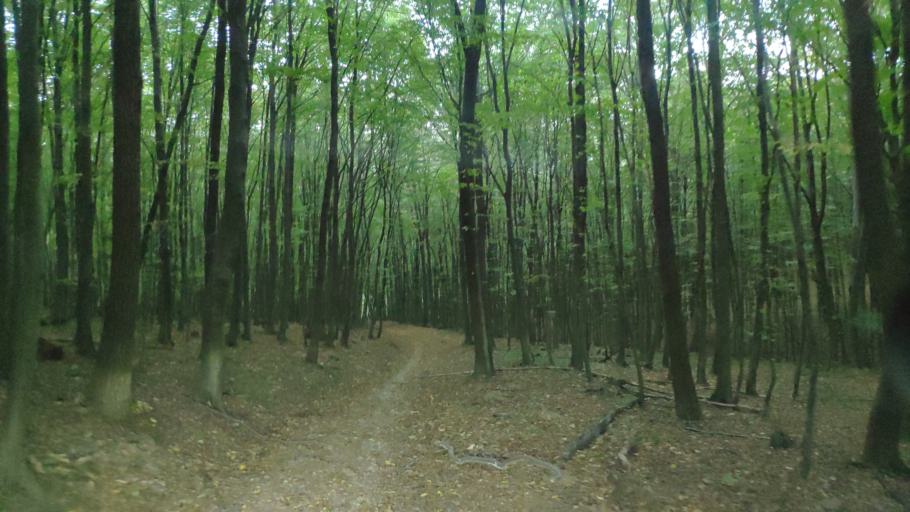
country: SK
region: Kosicky
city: Kosice
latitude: 48.6990
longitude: 21.1992
